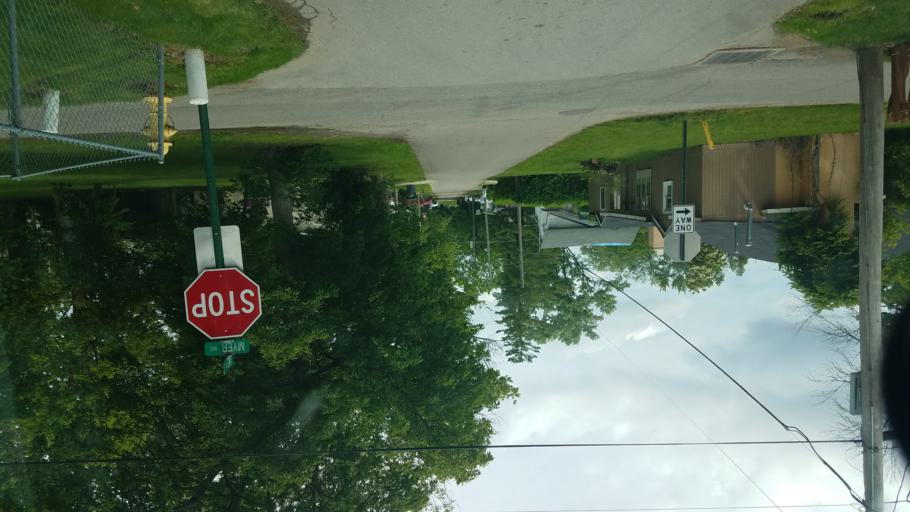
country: US
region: Ohio
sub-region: Licking County
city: Buckeye Lake
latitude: 39.9344
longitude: -82.4742
